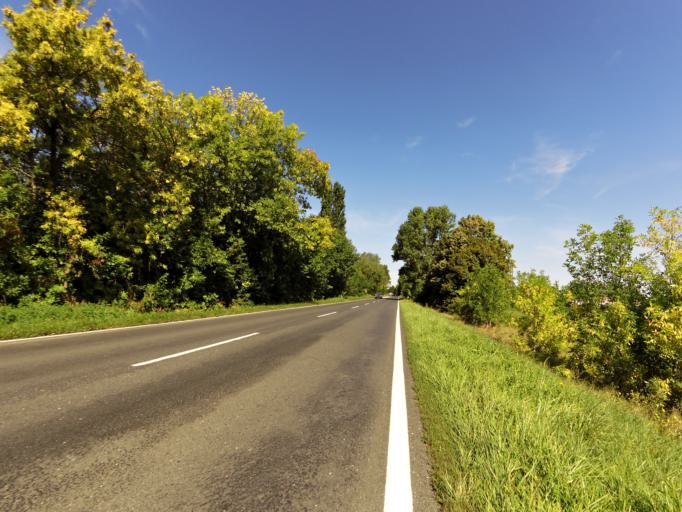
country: HU
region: Veszprem
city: Tapolca
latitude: 46.8313
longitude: 17.3768
